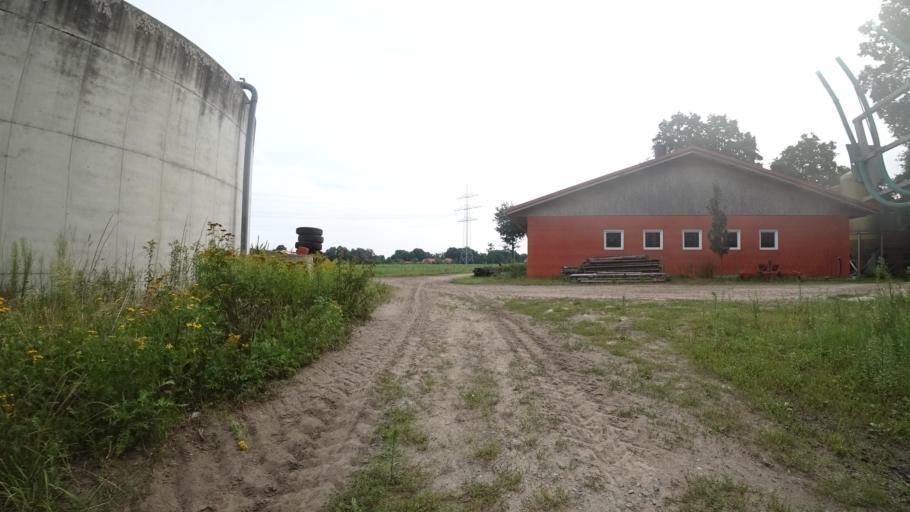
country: DE
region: North Rhine-Westphalia
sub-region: Regierungsbezirk Detmold
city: Guetersloh
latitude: 51.9288
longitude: 8.4037
